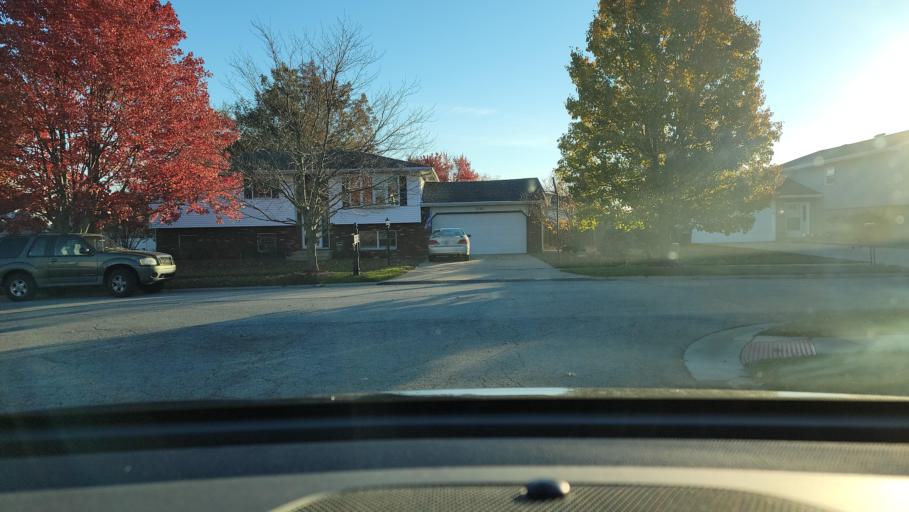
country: US
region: Indiana
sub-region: Porter County
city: Portage
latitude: 41.5602
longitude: -87.1679
